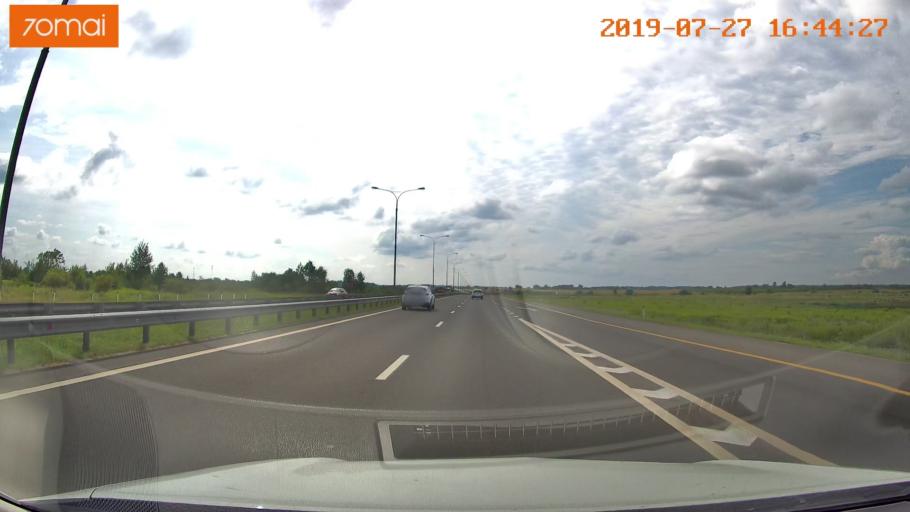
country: RU
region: Kaliningrad
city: Gvardeysk
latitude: 54.6726
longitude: 21.0772
